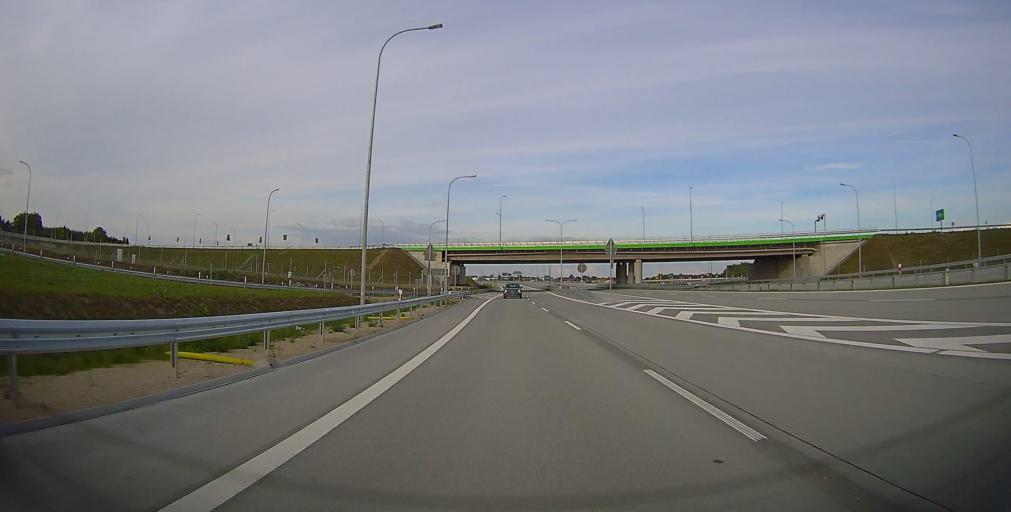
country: PL
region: Masovian Voivodeship
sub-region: Powiat piaseczynski
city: Mysiadlo
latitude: 52.1155
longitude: 20.9844
